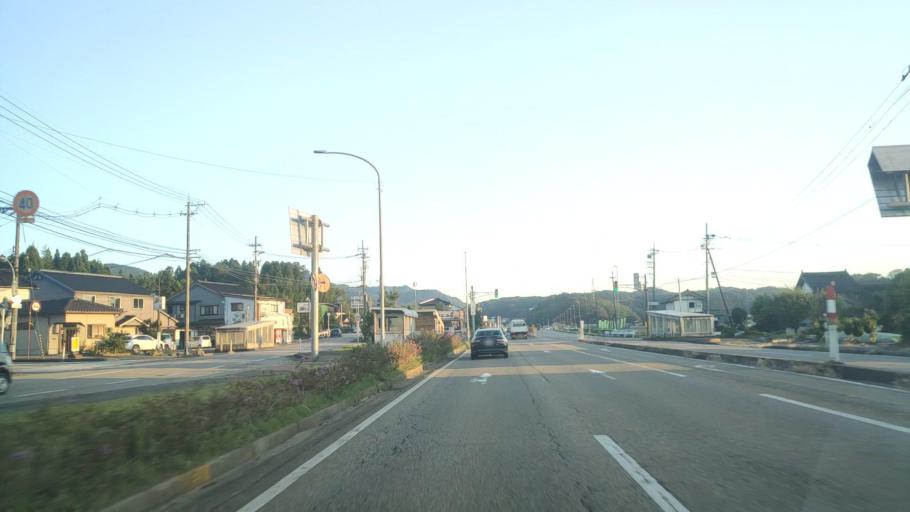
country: JP
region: Toyama
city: Himi
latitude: 36.8170
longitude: 136.9954
